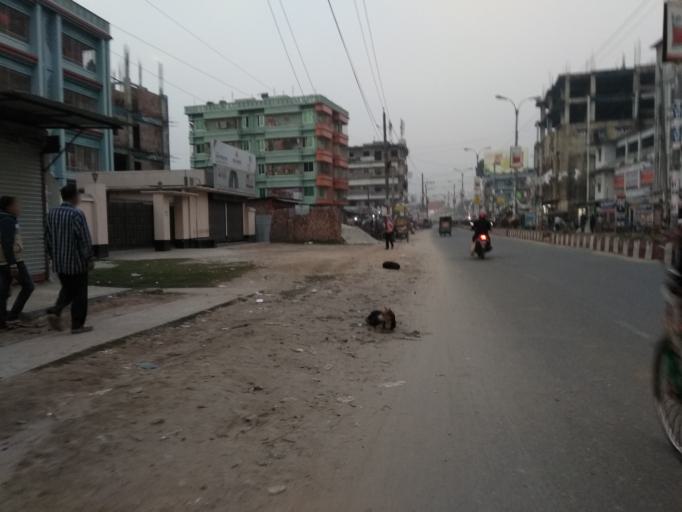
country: BD
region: Rangpur Division
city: Rangpur
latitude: 25.7319
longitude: 89.2547
